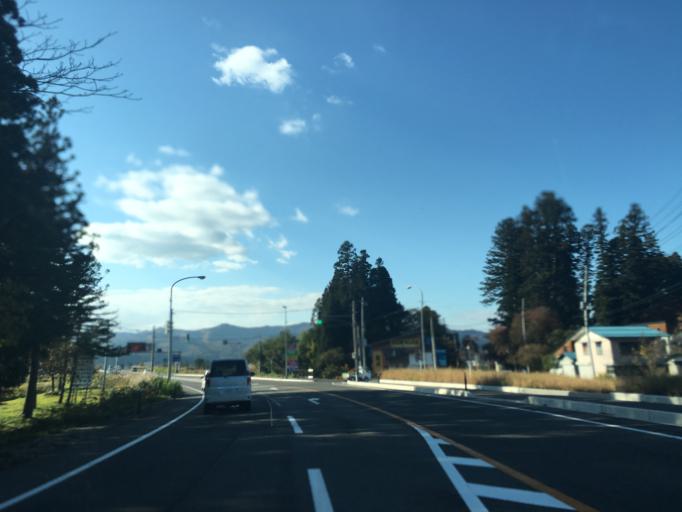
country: JP
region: Fukushima
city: Kitakata
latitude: 37.5782
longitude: 139.6593
